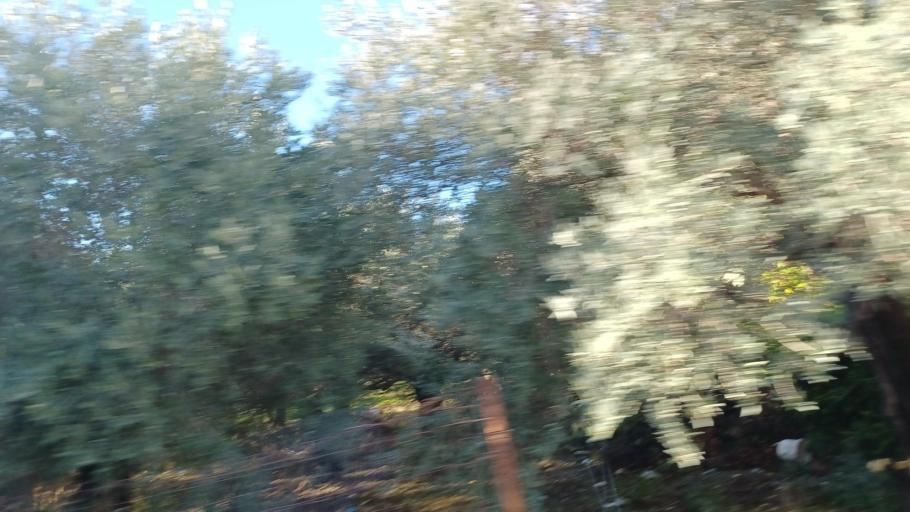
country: CY
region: Limassol
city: Pachna
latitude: 34.8521
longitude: 32.7425
